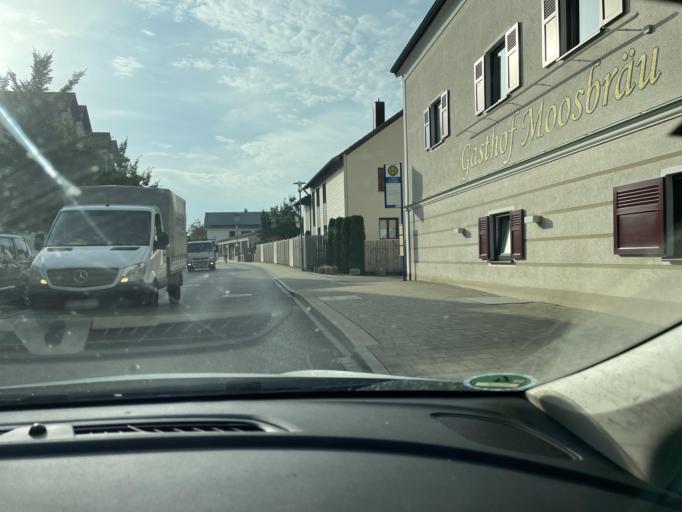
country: DE
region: Bavaria
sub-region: Swabia
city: Aindling
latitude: 48.5131
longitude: 10.9582
